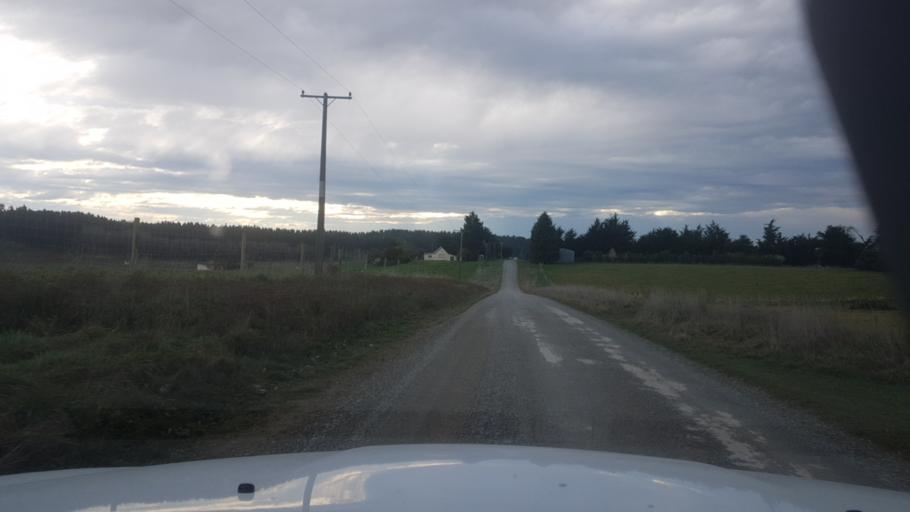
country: NZ
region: Canterbury
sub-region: Timaru District
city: Pleasant Point
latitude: -44.3343
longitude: 171.1538
